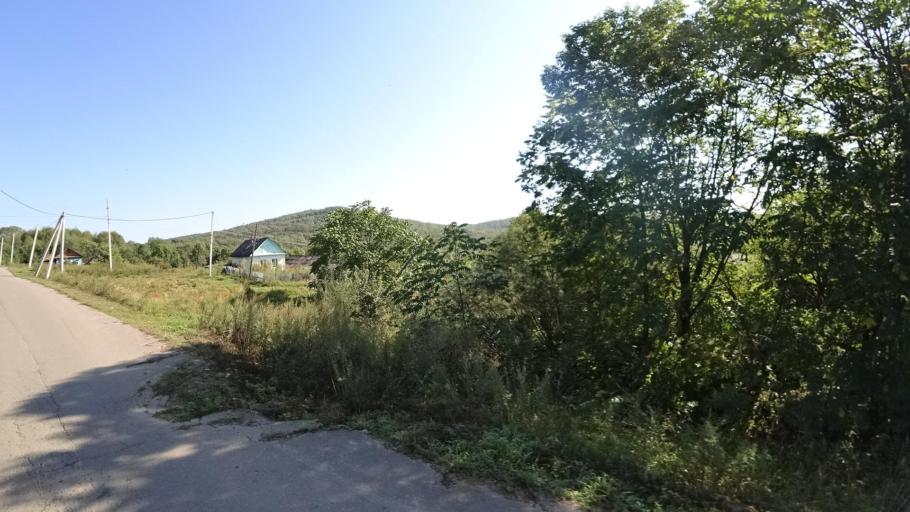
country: RU
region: Jewish Autonomous Oblast
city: Bira
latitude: 49.0107
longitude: 132.4736
